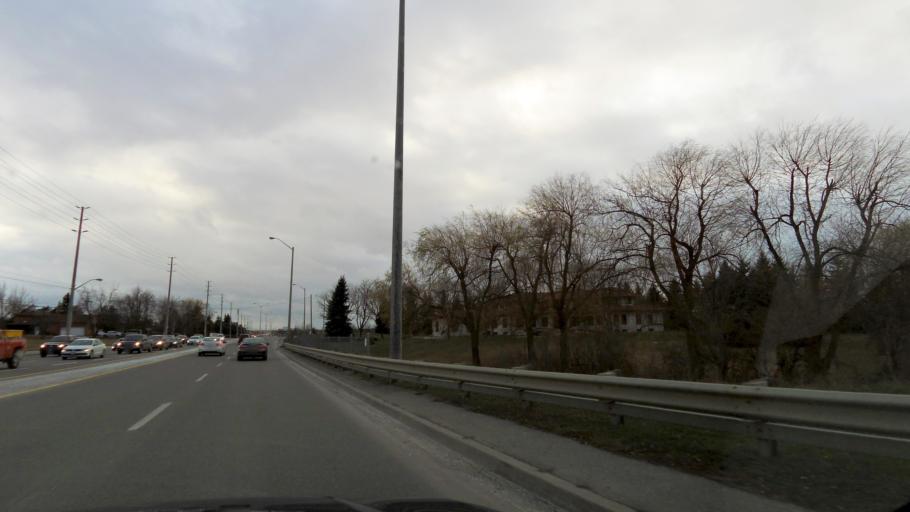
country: CA
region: Ontario
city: Brampton
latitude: 43.7915
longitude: -79.6905
